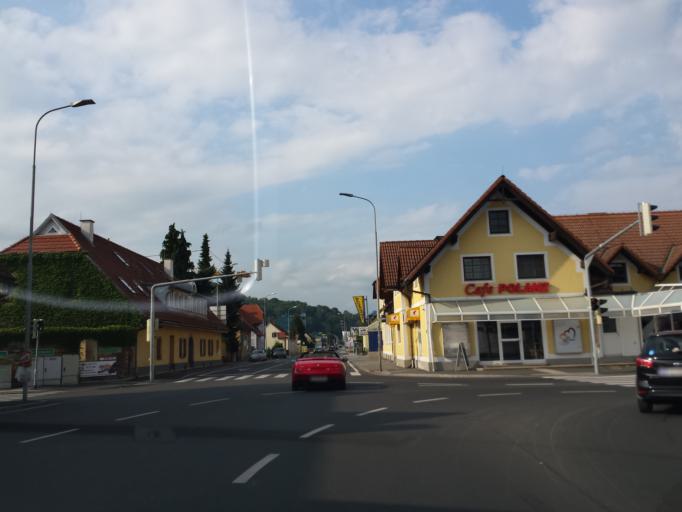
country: AT
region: Styria
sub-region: Politischer Bezirk Graz-Umgebung
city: Seiersberg
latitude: 47.0098
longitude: 15.3991
